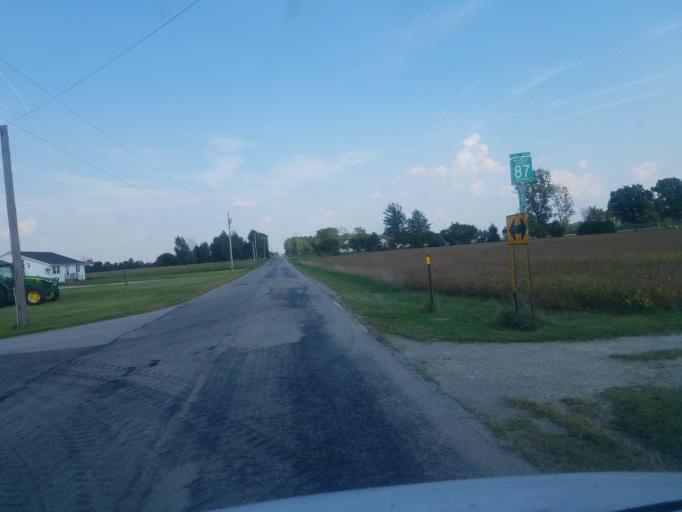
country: US
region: Ohio
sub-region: Wyandot County
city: Carey
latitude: 40.9050
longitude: -83.4672
